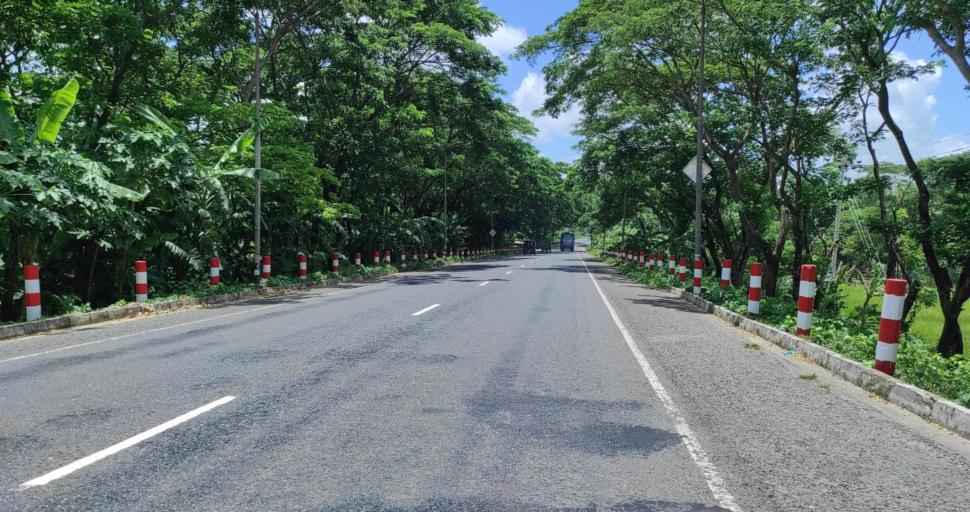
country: BD
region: Barisal
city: Barisal
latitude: 22.8226
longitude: 90.2663
